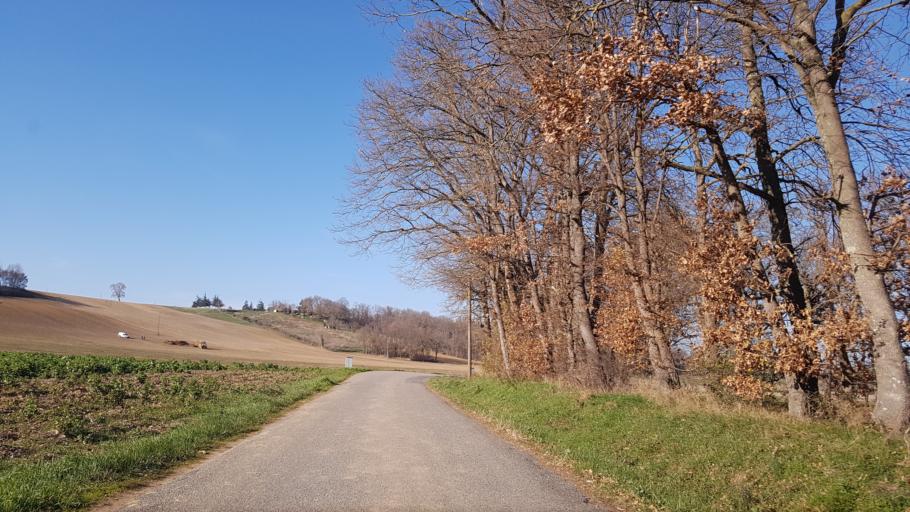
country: FR
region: Midi-Pyrenees
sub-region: Departement de l'Ariege
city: La Tour-du-Crieu
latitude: 43.1314
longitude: 1.7156
